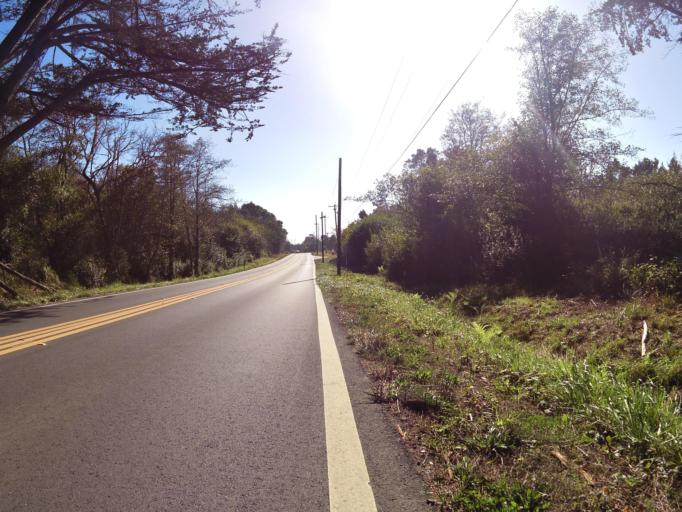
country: US
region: California
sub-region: Mendocino County
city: Fort Bragg
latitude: 39.4804
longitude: -123.7956
